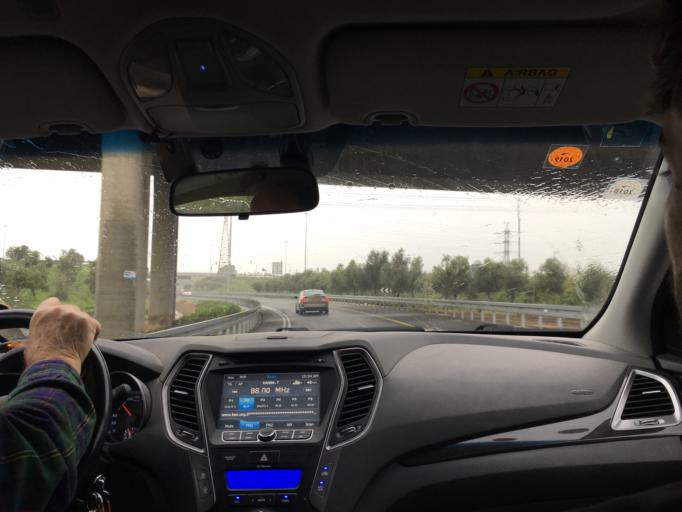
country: IL
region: Central District
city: Rosh Ha'Ayin
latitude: 32.1155
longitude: 34.9402
